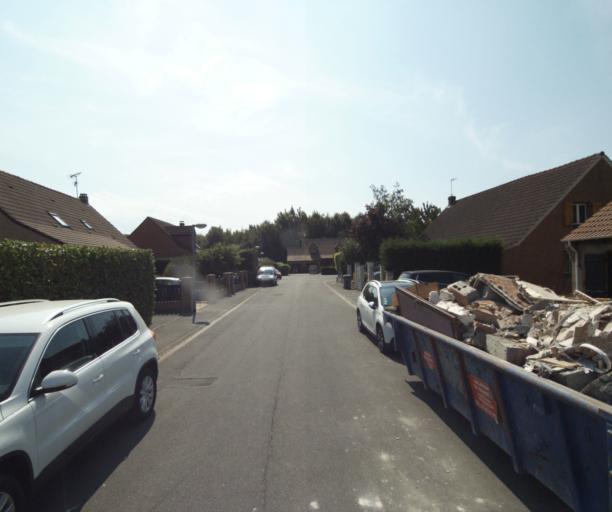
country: FR
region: Nord-Pas-de-Calais
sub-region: Departement du Nord
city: Comines
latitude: 50.7527
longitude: 3.0029
